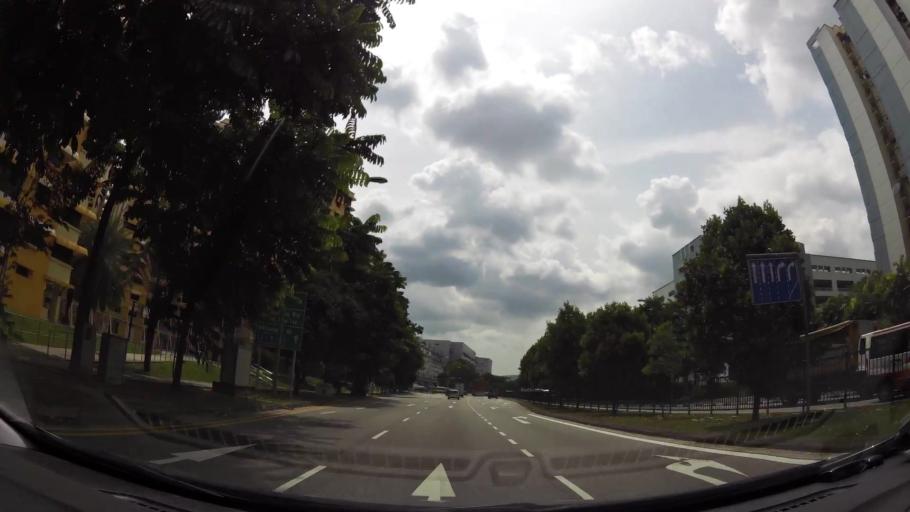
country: MY
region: Johor
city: Johor Bahru
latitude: 1.3358
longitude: 103.6962
